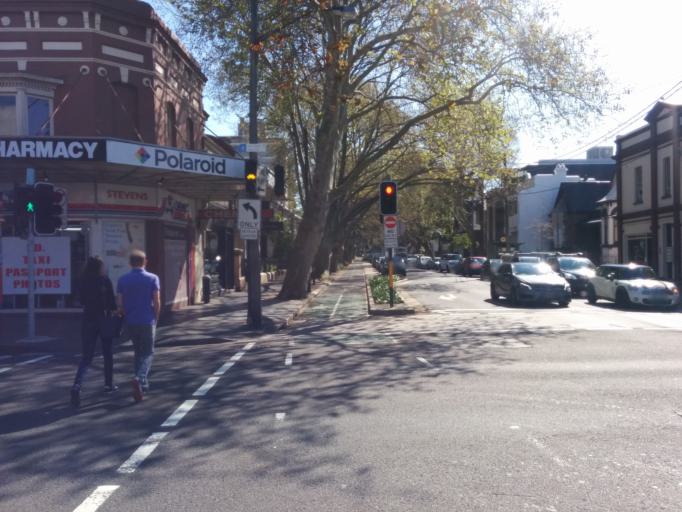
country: AU
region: New South Wales
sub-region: City of Sydney
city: Redfern
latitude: -33.8918
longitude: 151.2145
